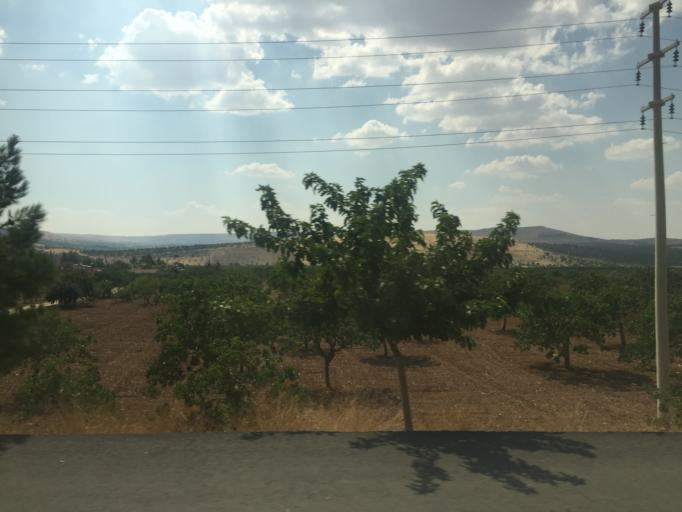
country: TR
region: Sanliurfa
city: Sanliurfa
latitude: 37.2411
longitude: 38.7939
